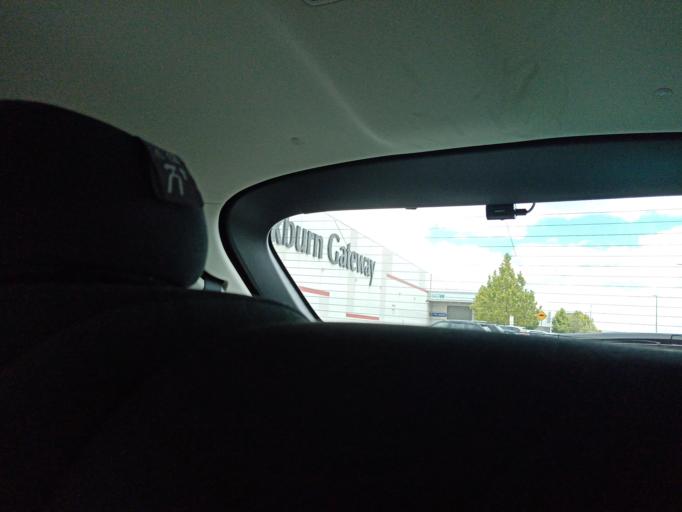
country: AU
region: Western Australia
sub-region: City of Cockburn
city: Success
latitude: -32.1318
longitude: 115.8588
